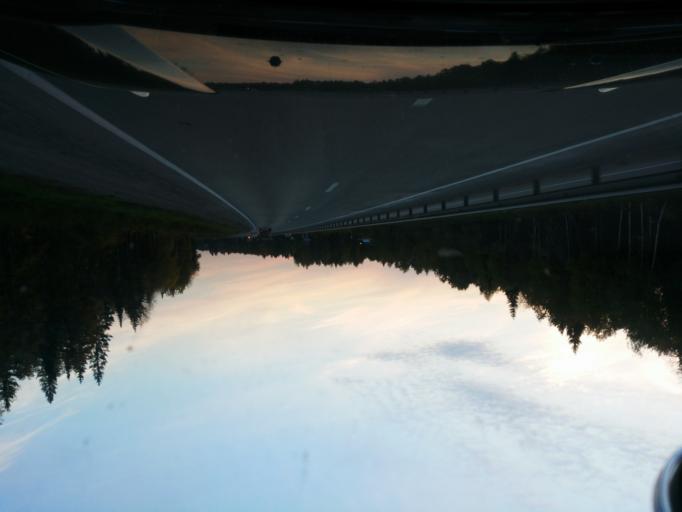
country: RU
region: Perm
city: Polazna
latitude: 58.2452
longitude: 56.4147
